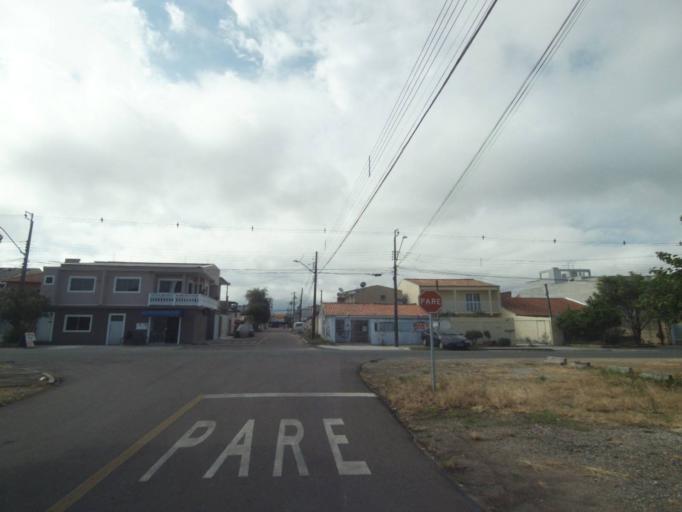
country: BR
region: Parana
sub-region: Pinhais
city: Pinhais
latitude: -25.4579
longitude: -49.2027
